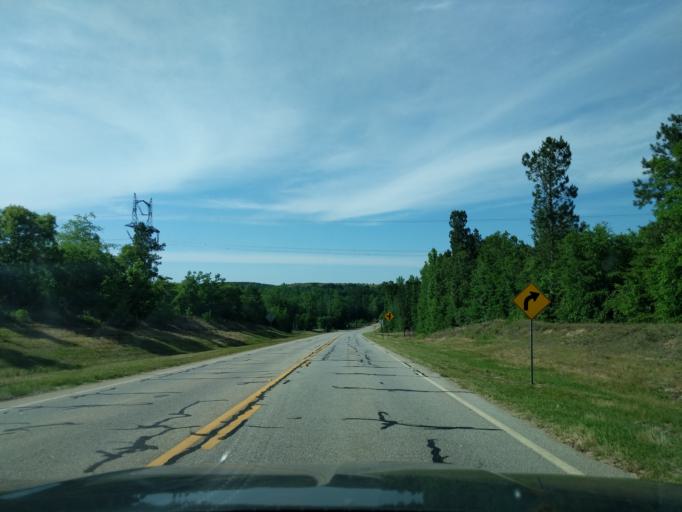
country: US
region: Georgia
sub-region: Jefferson County
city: Wrens
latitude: 33.2697
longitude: -82.3861
